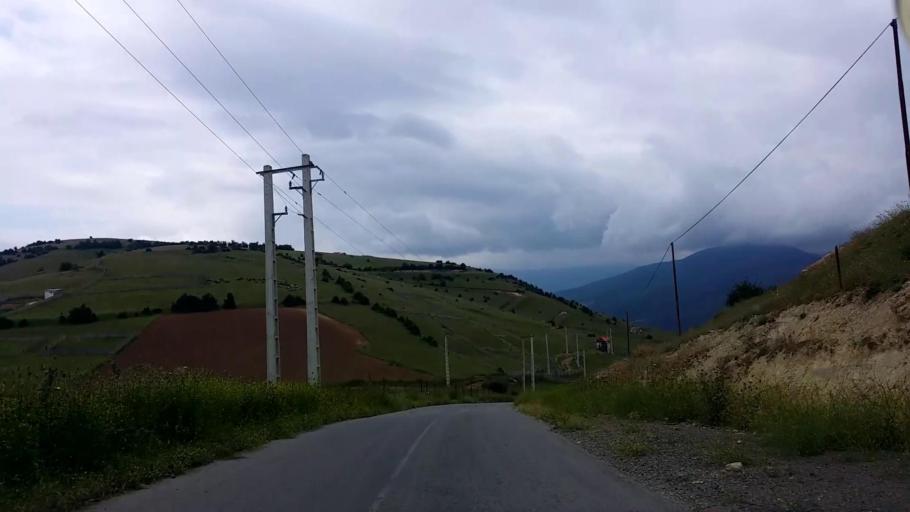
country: IR
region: Mazandaran
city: Chalus
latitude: 36.5280
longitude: 51.2682
